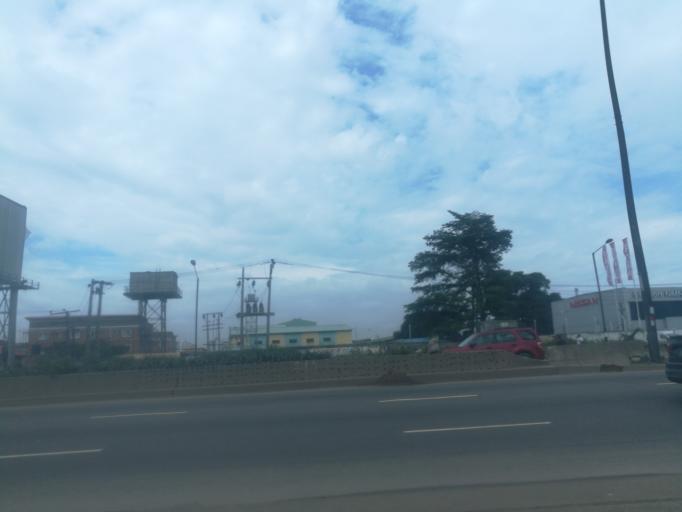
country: NG
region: Lagos
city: Somolu
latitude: 6.5528
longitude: 3.3742
